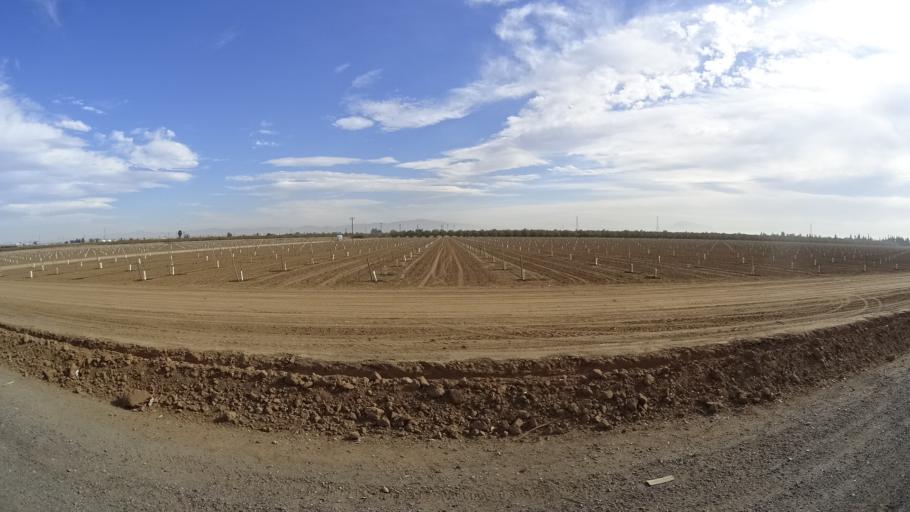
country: US
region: California
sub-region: Kern County
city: Greenacres
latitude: 35.4336
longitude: -119.0922
